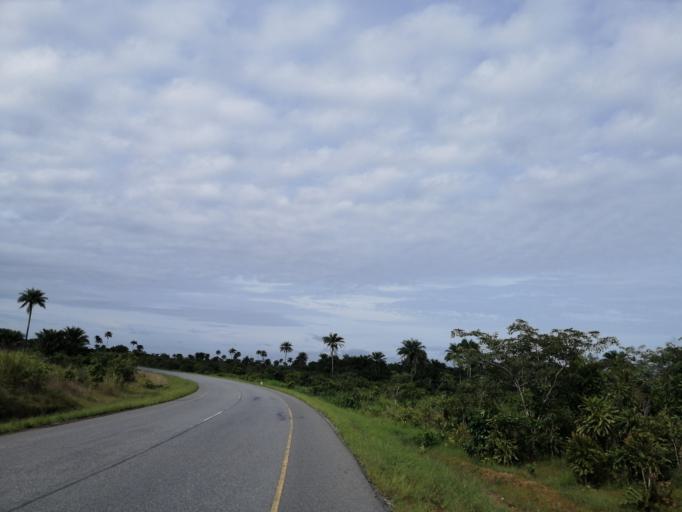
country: SL
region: Northern Province
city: Port Loko
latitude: 8.7809
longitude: -12.8568
